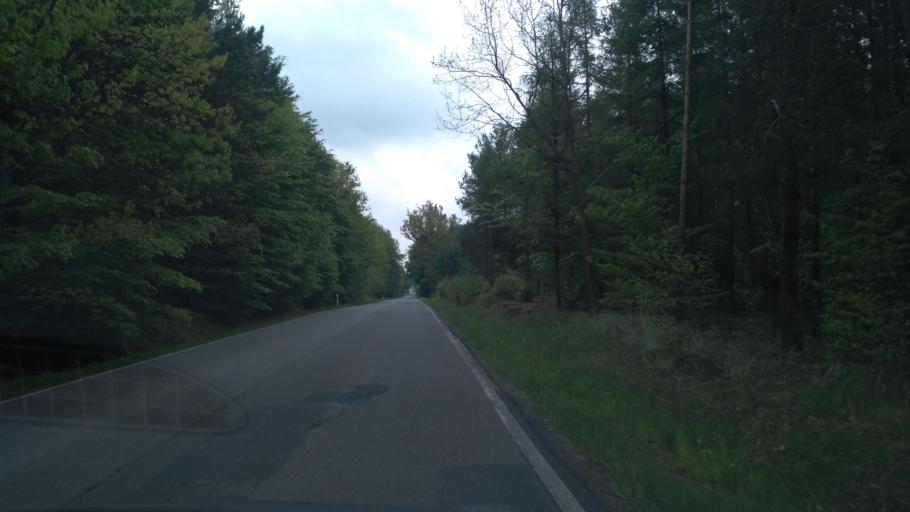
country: PL
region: Subcarpathian Voivodeship
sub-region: Powiat kolbuszowski
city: Kolbuszowa
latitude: 50.1718
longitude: 21.7599
